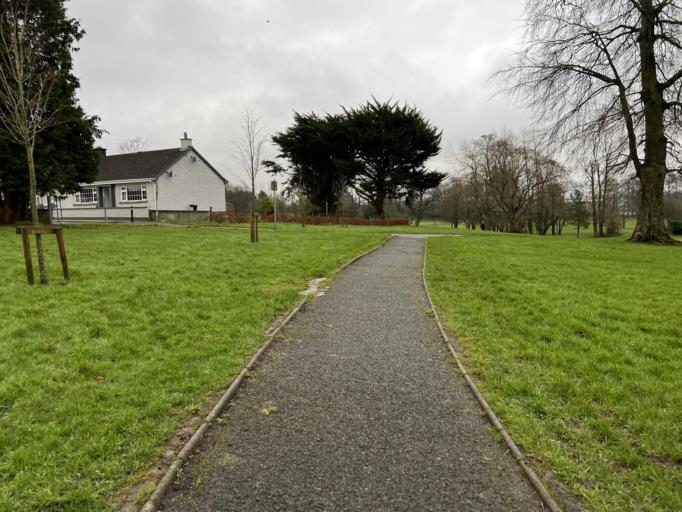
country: IE
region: Connaught
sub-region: County Galway
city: Tuam
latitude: 53.5194
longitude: -8.8509
